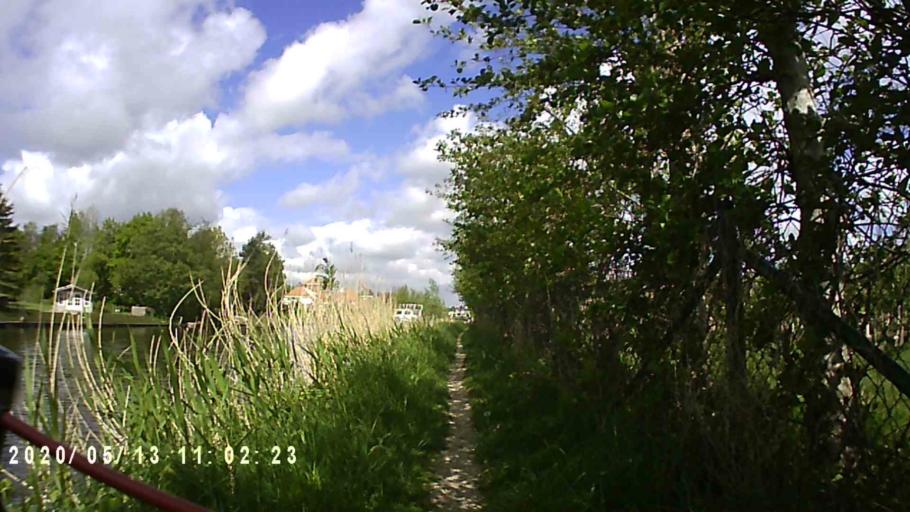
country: NL
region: Groningen
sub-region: Gemeente Zuidhorn
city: Grijpskerk
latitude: 53.2849
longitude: 6.3270
